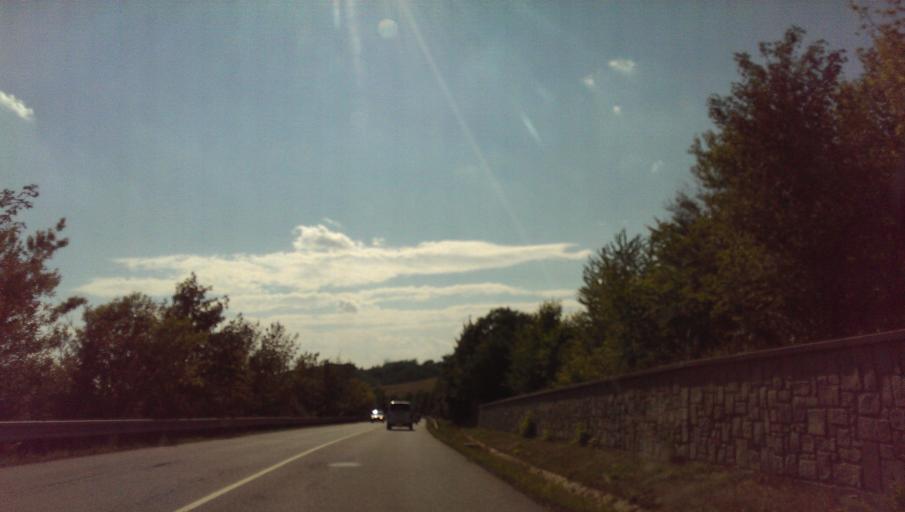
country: CZ
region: Zlin
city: Prusinovice
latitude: 49.3638
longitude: 17.6230
